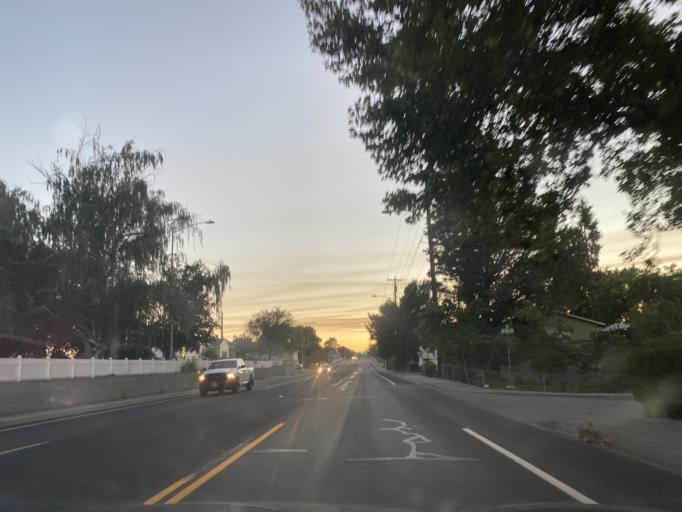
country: US
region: Washington
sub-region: Benton County
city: Kennewick
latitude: 46.1987
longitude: -119.1498
